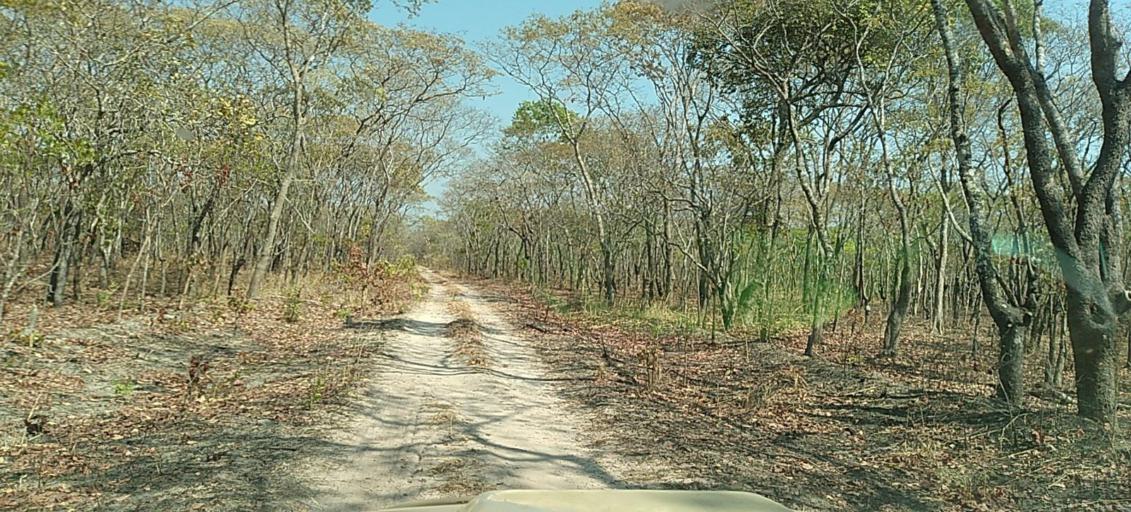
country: ZM
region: North-Western
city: Kalengwa
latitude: -13.3279
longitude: 24.8341
